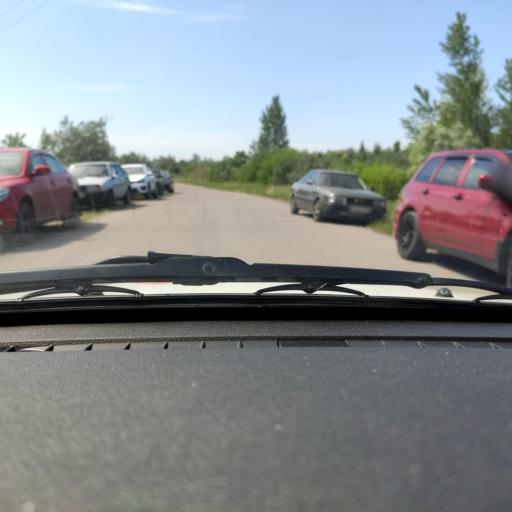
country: RU
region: Voronezj
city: Devitsa
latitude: 51.6232
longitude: 38.9596
